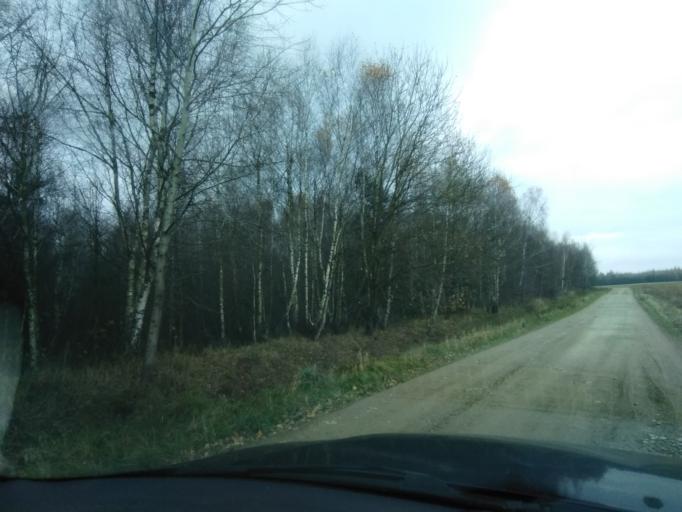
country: PL
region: Subcarpathian Voivodeship
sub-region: Powiat strzyzowski
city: Wysoka Strzyzowska
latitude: 49.7997
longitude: 21.7815
